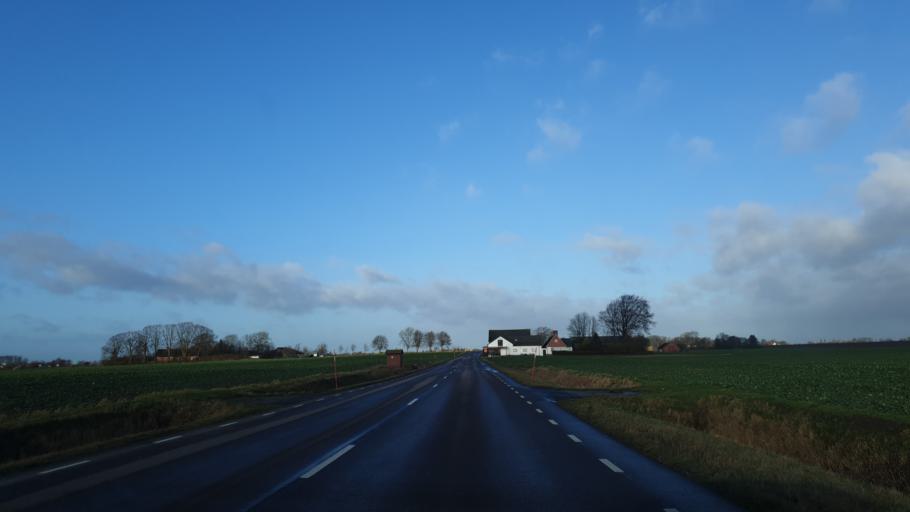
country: SE
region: Skane
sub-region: Vellinge Kommun
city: Vellinge
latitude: 55.4848
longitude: 13.0253
